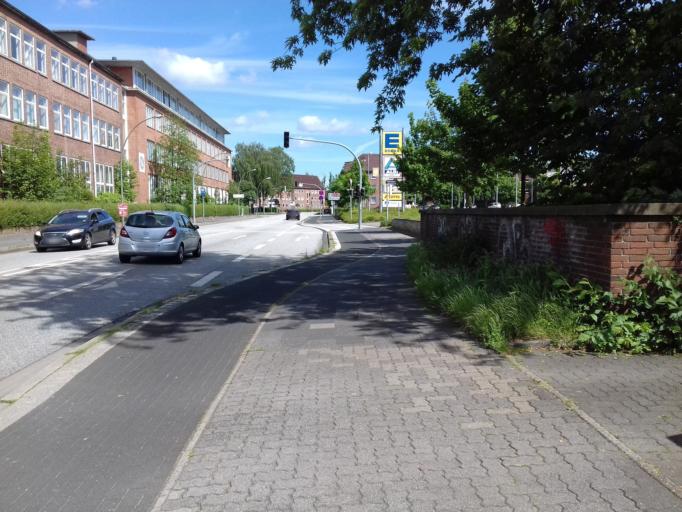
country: DE
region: Schleswig-Holstein
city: Neumunster
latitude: 54.0800
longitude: 9.9937
